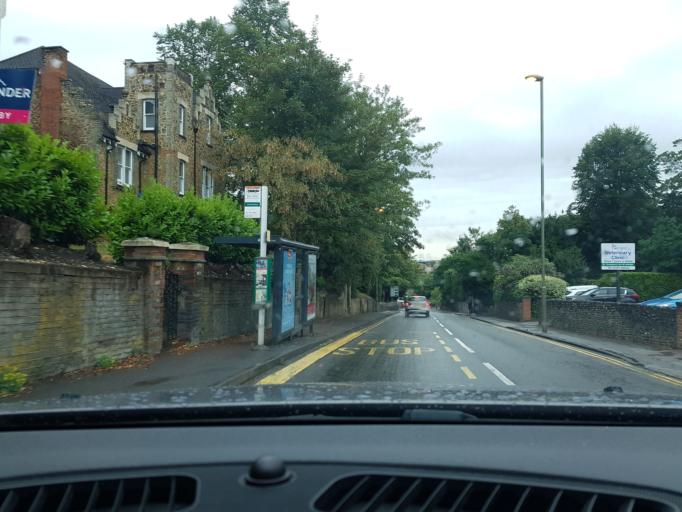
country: GB
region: England
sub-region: Surrey
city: Guildford
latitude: 51.2379
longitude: -0.5591
